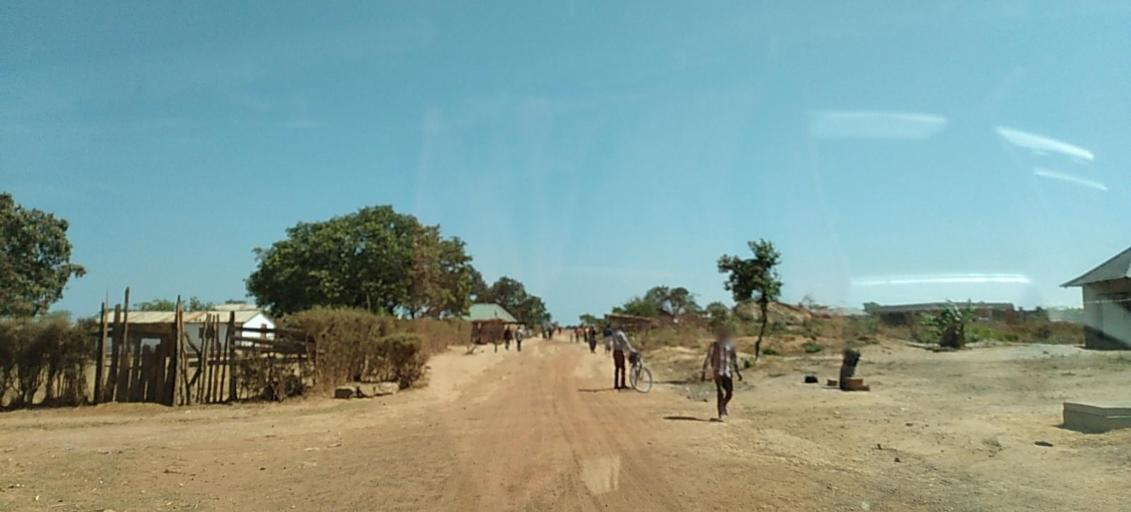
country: ZM
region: Copperbelt
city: Chililabombwe
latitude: -12.3242
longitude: 27.8603
